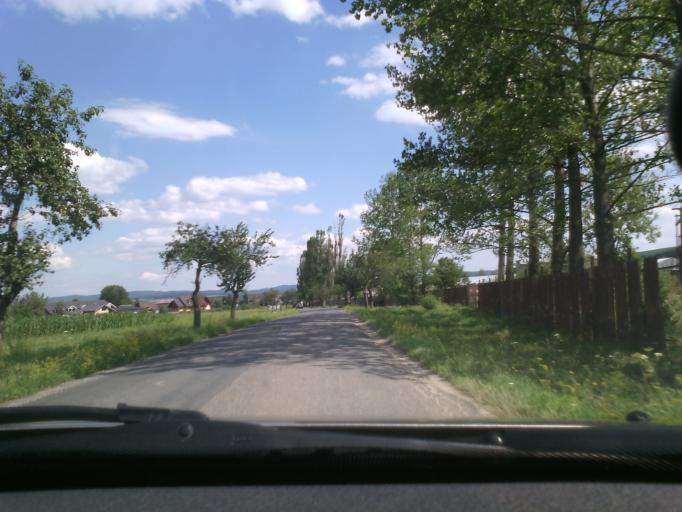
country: SK
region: Presovsky
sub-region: Okres Poprad
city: Poprad
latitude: 49.1211
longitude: 20.3466
